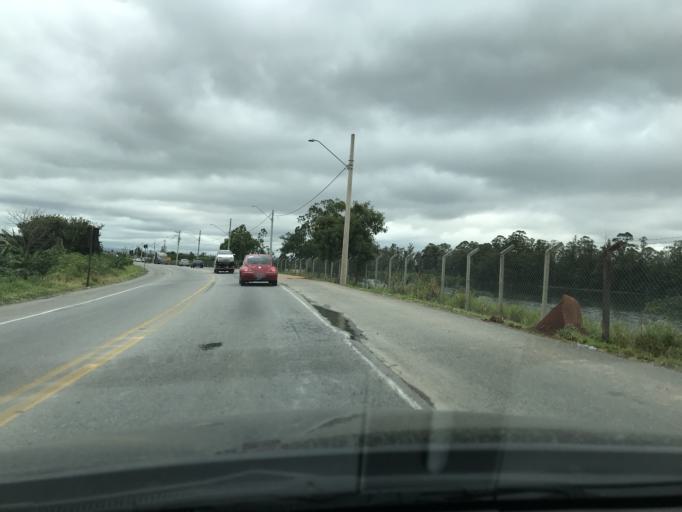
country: BR
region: Sao Paulo
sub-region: Itaquaquecetuba
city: Itaquaquecetuba
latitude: -23.4895
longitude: -46.3276
